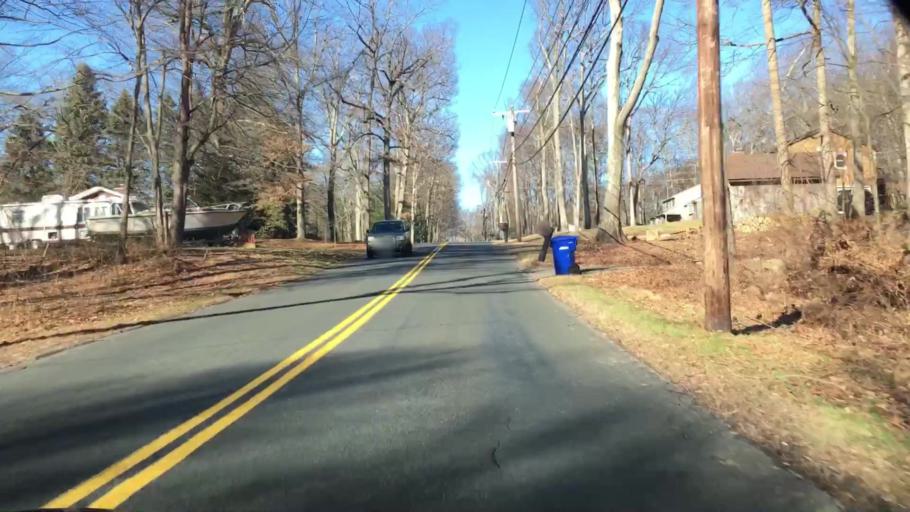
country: US
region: Connecticut
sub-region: Tolland County
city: Crystal Lake
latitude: 41.9402
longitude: -72.3907
